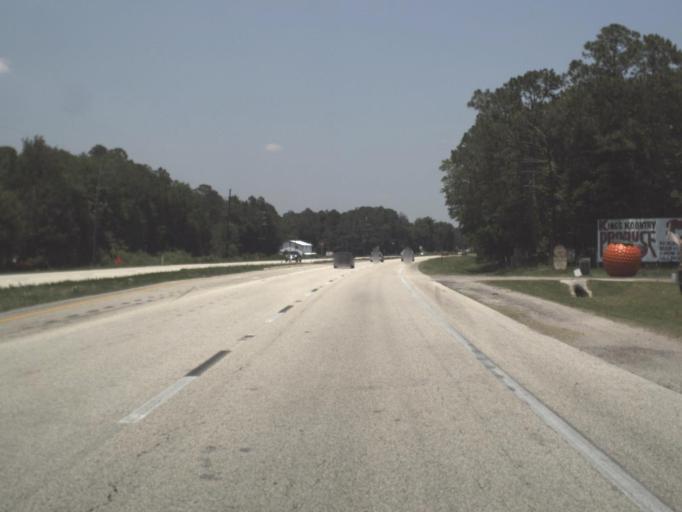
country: US
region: Florida
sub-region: Bradford County
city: Starke
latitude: 29.9796
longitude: -82.0994
